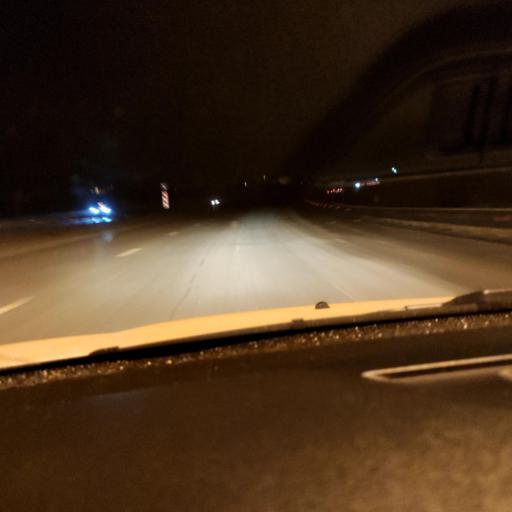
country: RU
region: Samara
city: Smyshlyayevka
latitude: 53.2664
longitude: 50.4041
